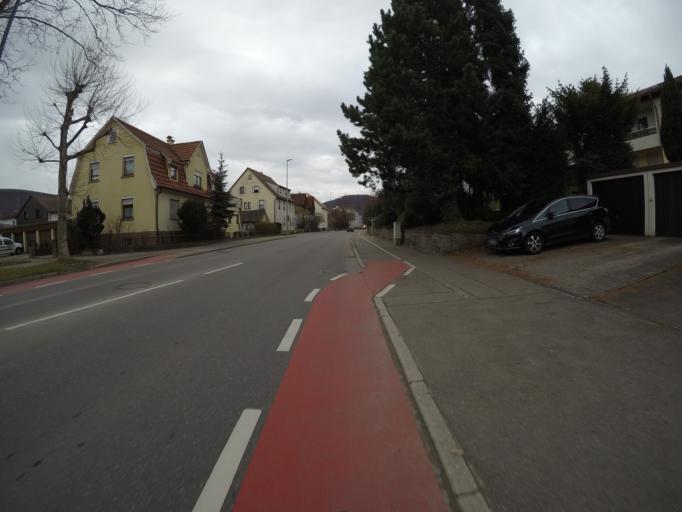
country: DE
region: Baden-Wuerttemberg
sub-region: Tuebingen Region
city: Pfullingen
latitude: 48.4707
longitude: 9.2209
